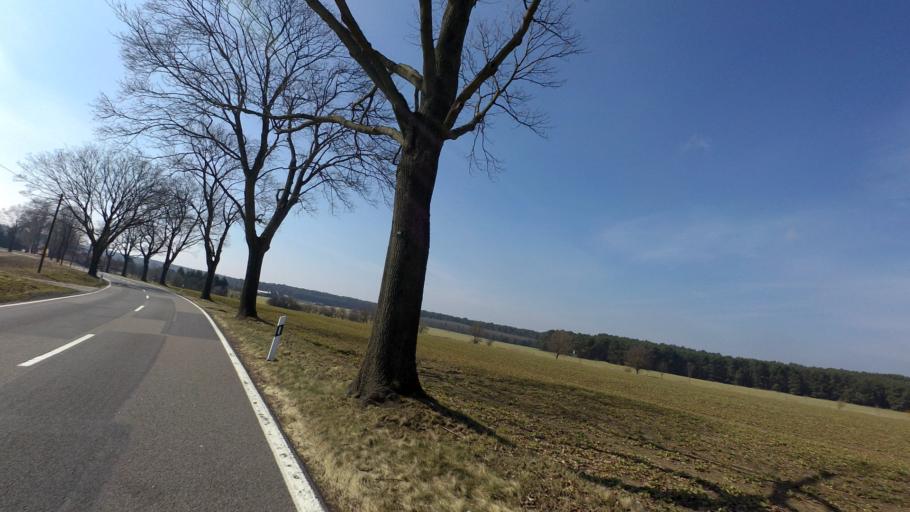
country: DE
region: Saxony-Anhalt
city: Nudersdorf
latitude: 51.9988
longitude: 12.5851
